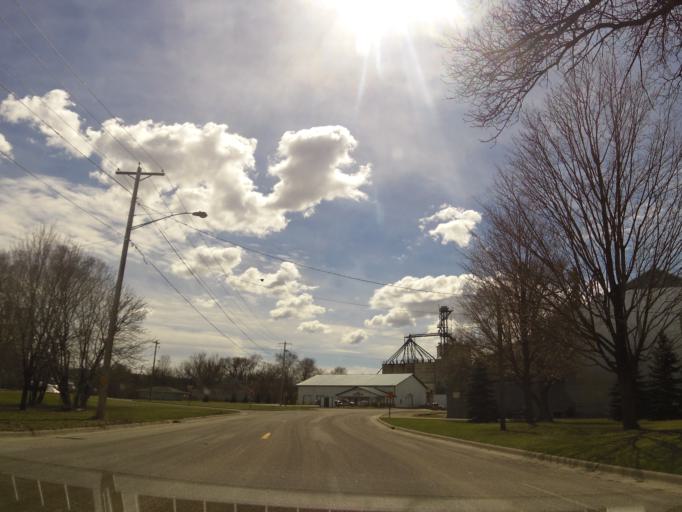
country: US
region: Minnesota
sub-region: Goodhue County
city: Cannon Falls
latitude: 44.5188
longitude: -92.9114
